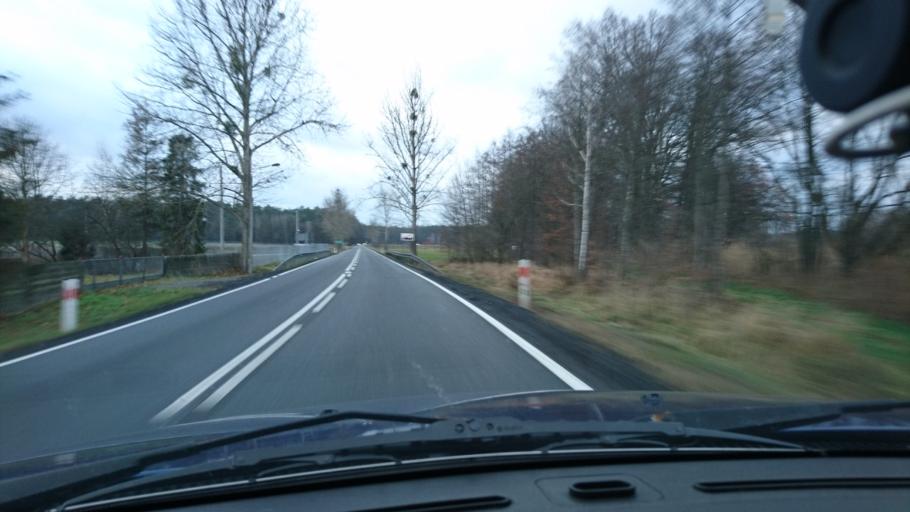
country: PL
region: Opole Voivodeship
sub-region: Powiat oleski
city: Olesno
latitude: 50.9165
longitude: 18.3463
